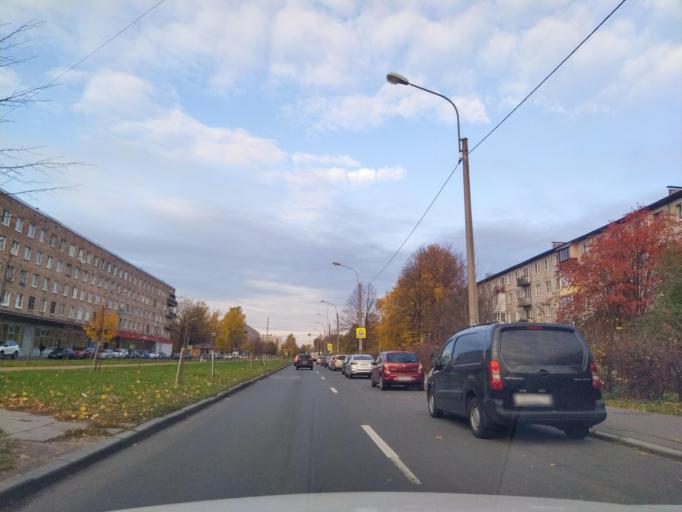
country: RU
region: Leningrad
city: Kalininskiy
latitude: 59.9725
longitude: 30.3986
